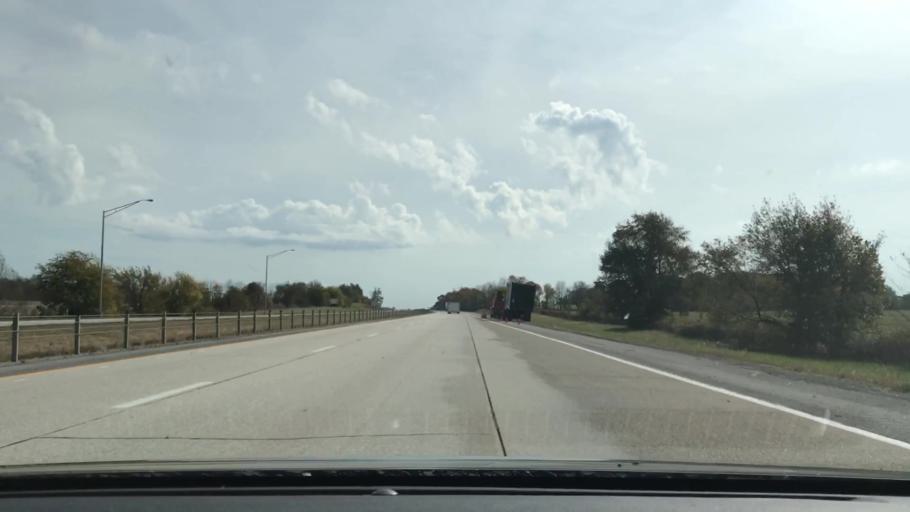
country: US
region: Kentucky
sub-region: Trigg County
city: Cadiz
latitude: 36.8793
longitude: -87.7312
